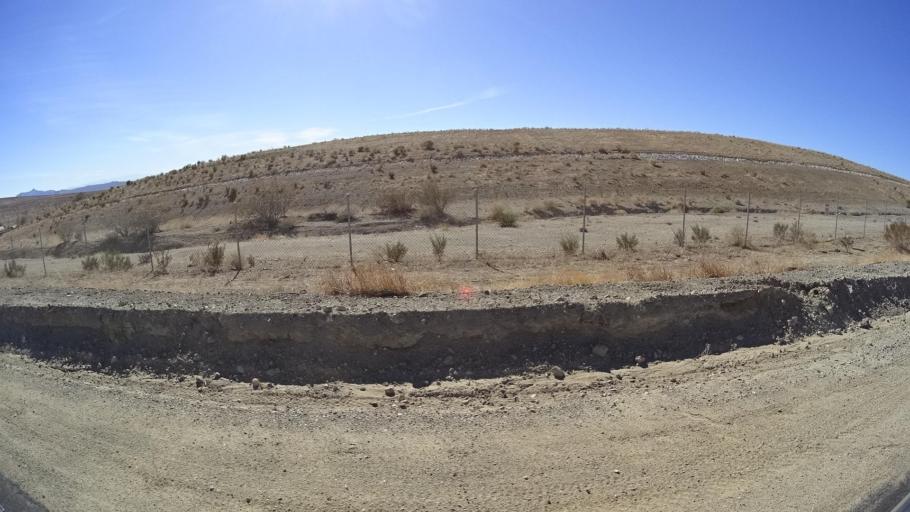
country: US
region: California
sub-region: Kern County
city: Ridgecrest
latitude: 35.3535
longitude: -117.6220
